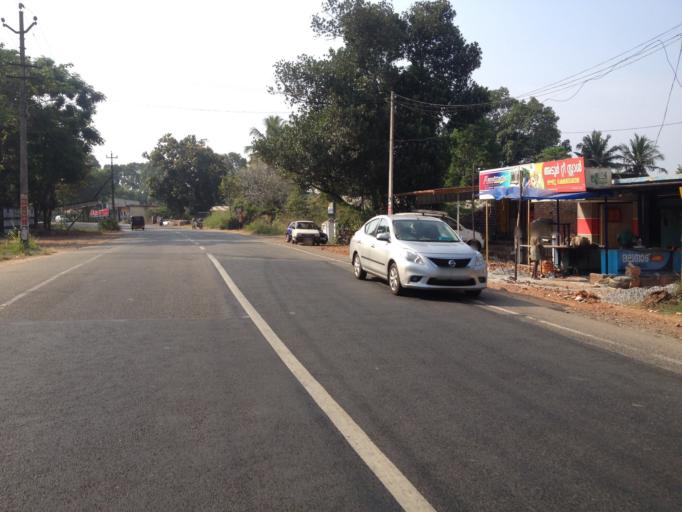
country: IN
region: Kerala
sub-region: Pattanamtitta
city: Adur
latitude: 9.1608
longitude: 76.7243
